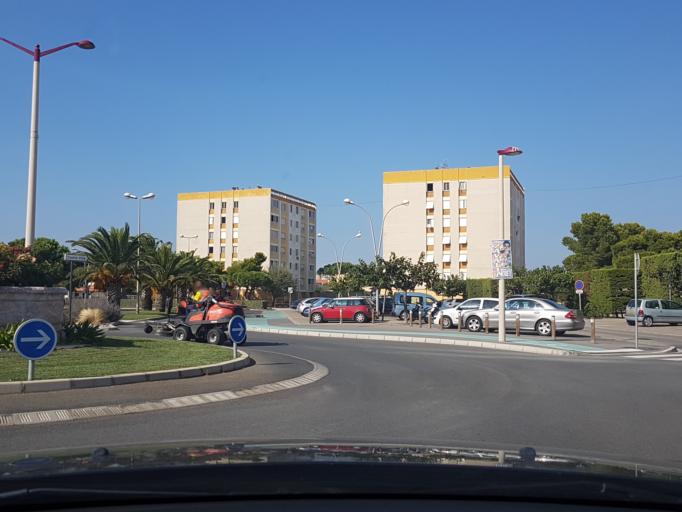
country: FR
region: Languedoc-Roussillon
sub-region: Departement de l'Aude
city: Port-la-Nouvelle
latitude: 43.0176
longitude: 3.0492
